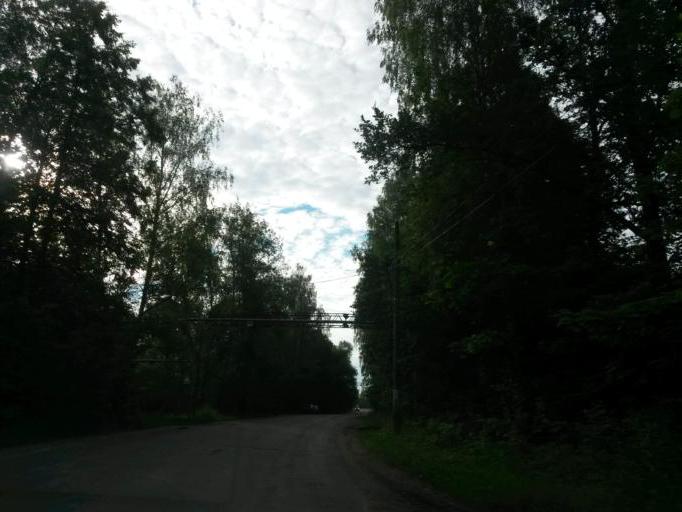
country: RU
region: Moskovskaya
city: Lyubuchany
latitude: 55.2491
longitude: 37.6337
